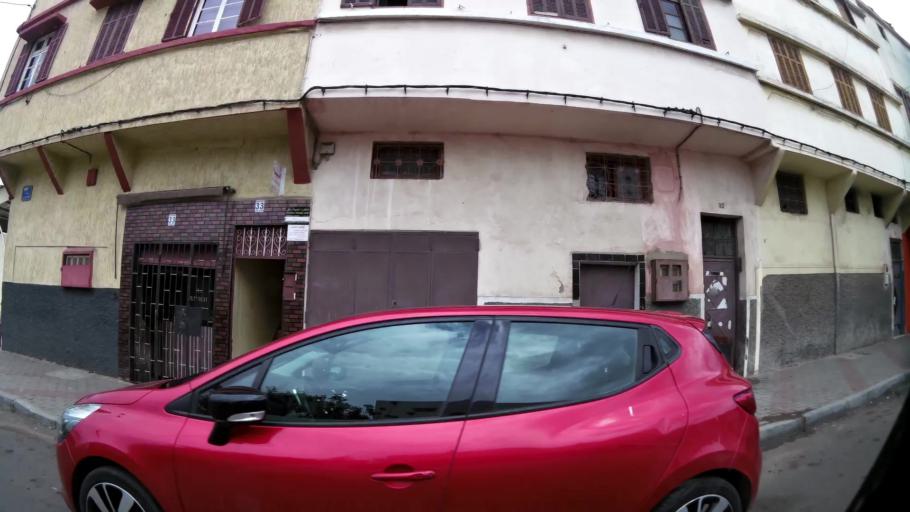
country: MA
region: Grand Casablanca
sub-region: Casablanca
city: Casablanca
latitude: 33.5838
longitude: -7.5649
